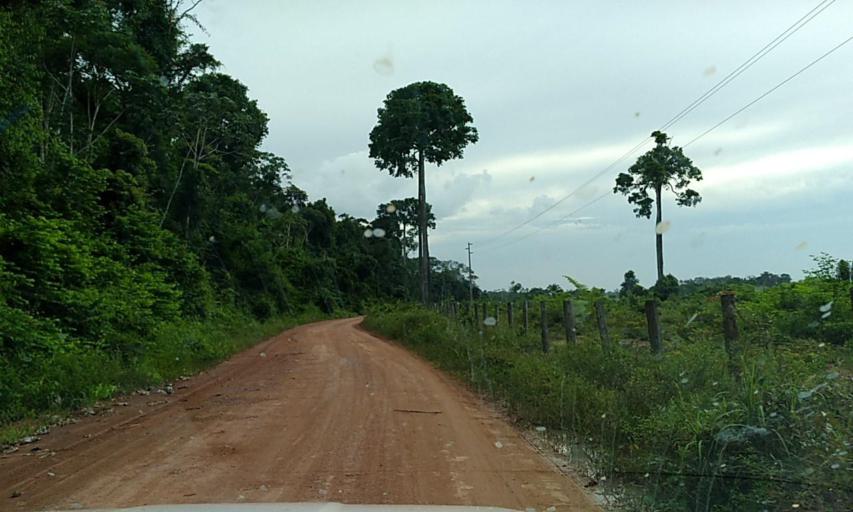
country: BR
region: Para
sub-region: Senador Jose Porfirio
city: Senador Jose Porfirio
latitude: -2.5456
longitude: -51.8610
